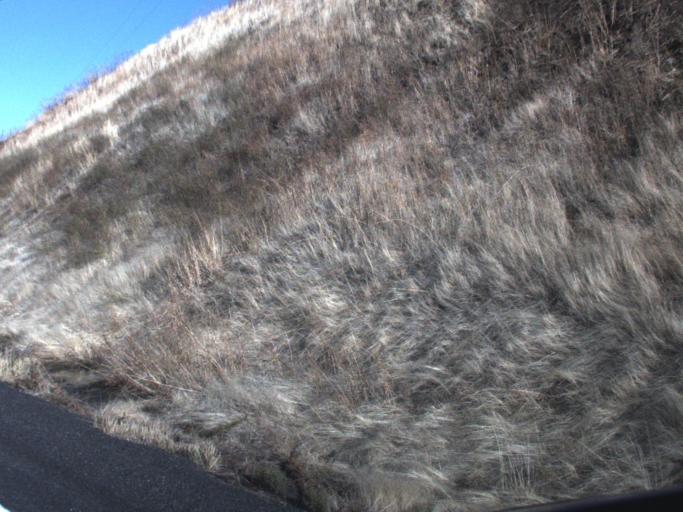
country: US
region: Washington
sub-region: Whitman County
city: Colfax
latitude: 46.7390
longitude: -117.3603
